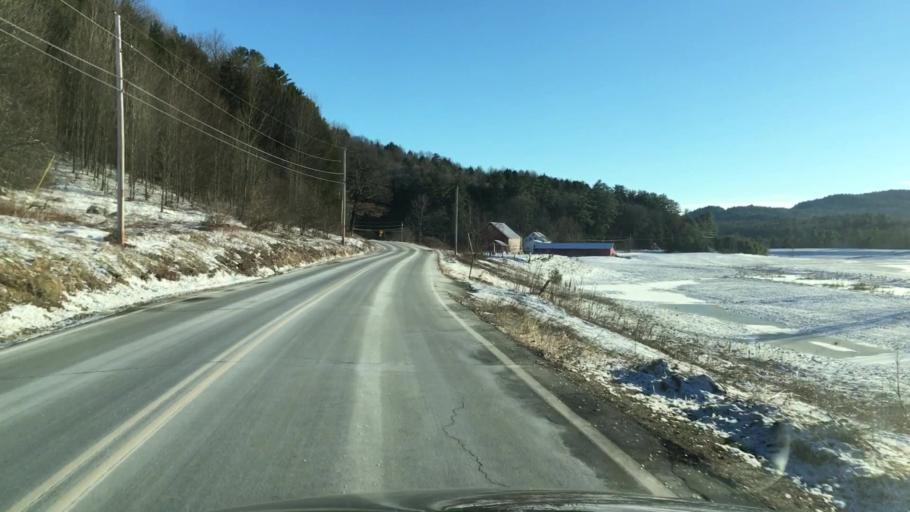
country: US
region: New Hampshire
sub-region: Grafton County
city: Woodsville
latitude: 44.1741
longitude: -72.0470
